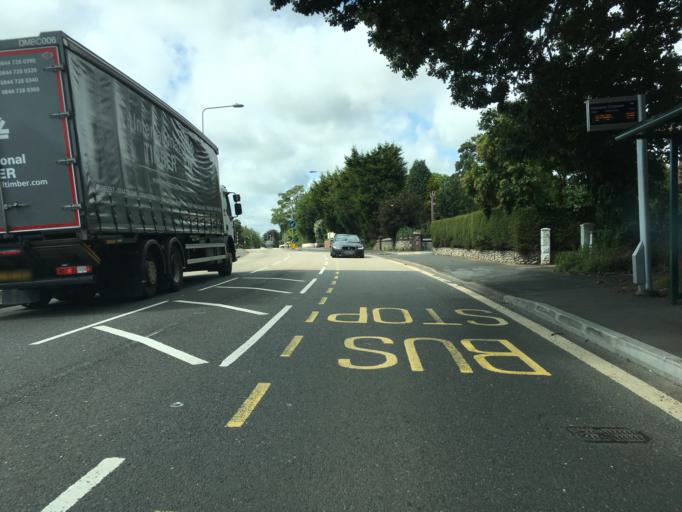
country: GB
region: England
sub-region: East Sussex
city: Bexhill-on-Sea
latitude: 50.8449
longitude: 0.4284
